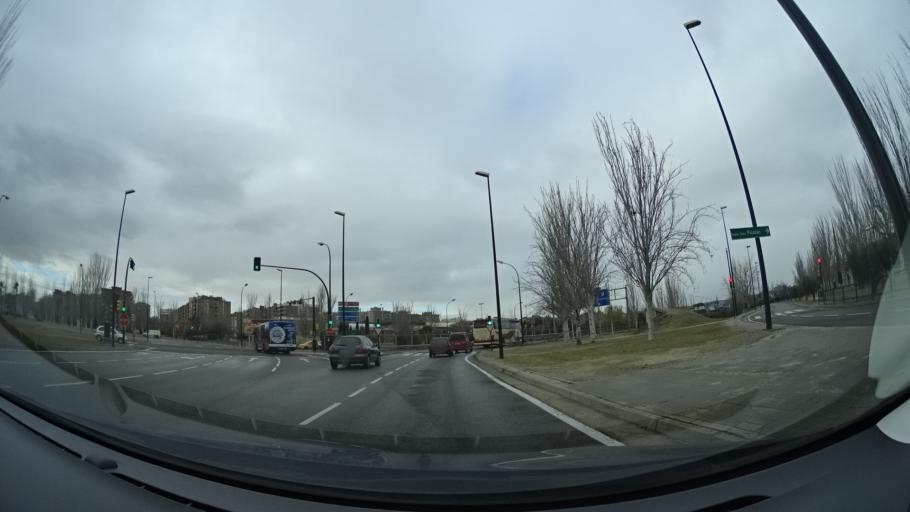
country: ES
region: Aragon
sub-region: Provincia de Zaragoza
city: Zaragoza
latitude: 41.6674
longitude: -0.8794
